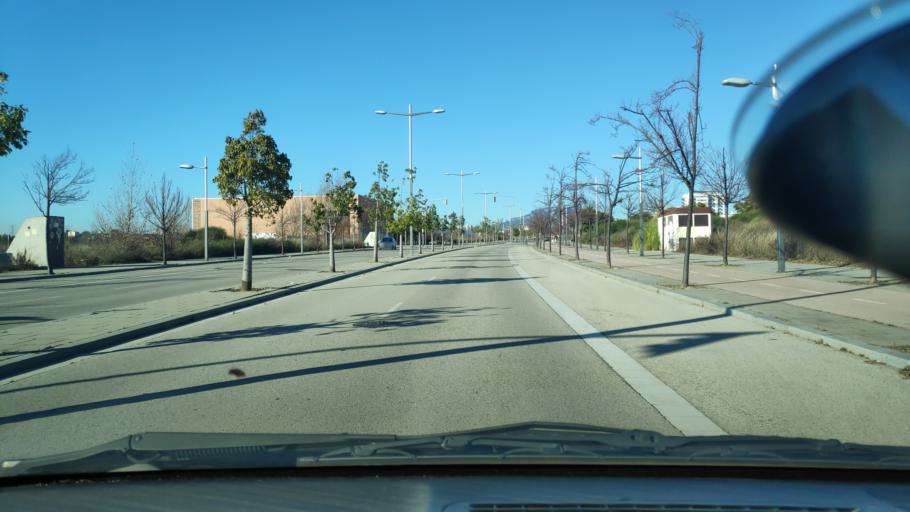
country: ES
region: Catalonia
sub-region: Provincia de Barcelona
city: Sant Quirze del Valles
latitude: 41.5443
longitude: 2.0810
